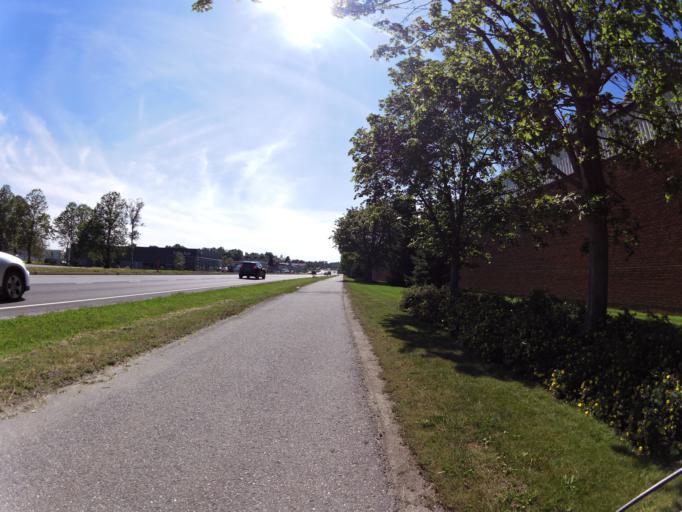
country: NO
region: Ostfold
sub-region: Fredrikstad
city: Fredrikstad
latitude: 59.2424
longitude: 10.9779
